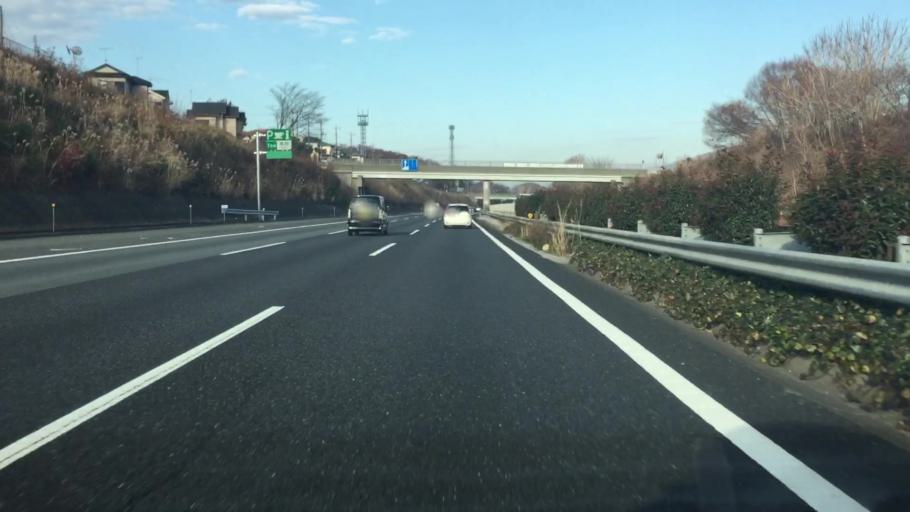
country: JP
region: Saitama
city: Yorii
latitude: 36.1641
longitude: 139.2039
